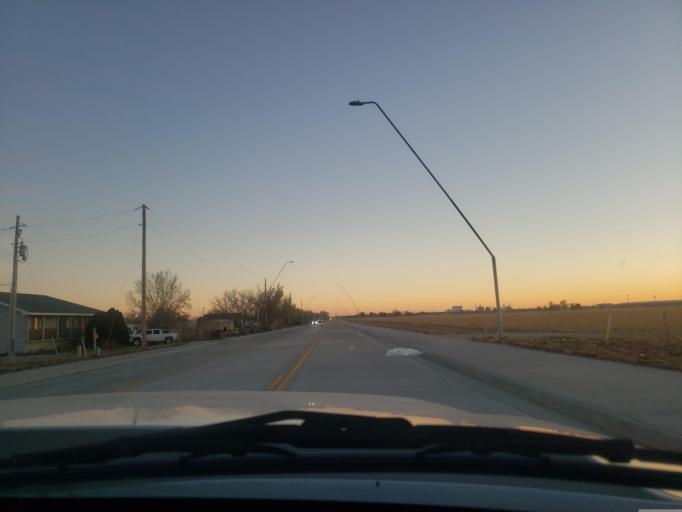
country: US
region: Kansas
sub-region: Finney County
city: Garden City
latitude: 37.9824
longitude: -100.8290
